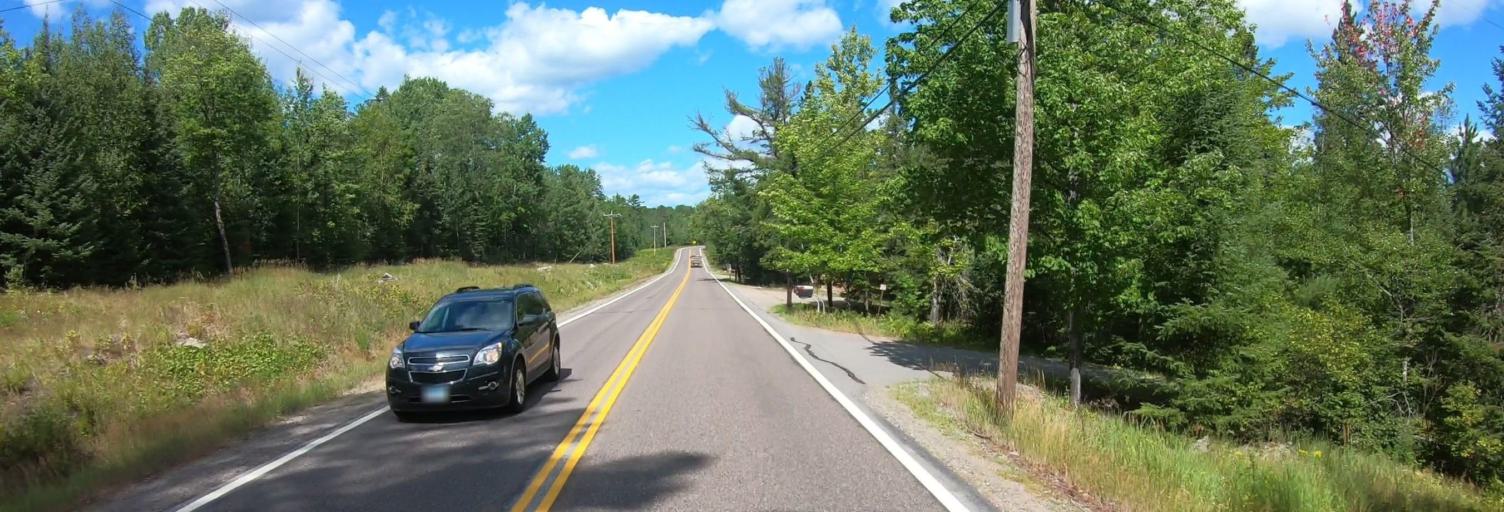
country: US
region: Minnesota
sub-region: Saint Louis County
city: Mountain Iron
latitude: 47.9320
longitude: -92.6743
